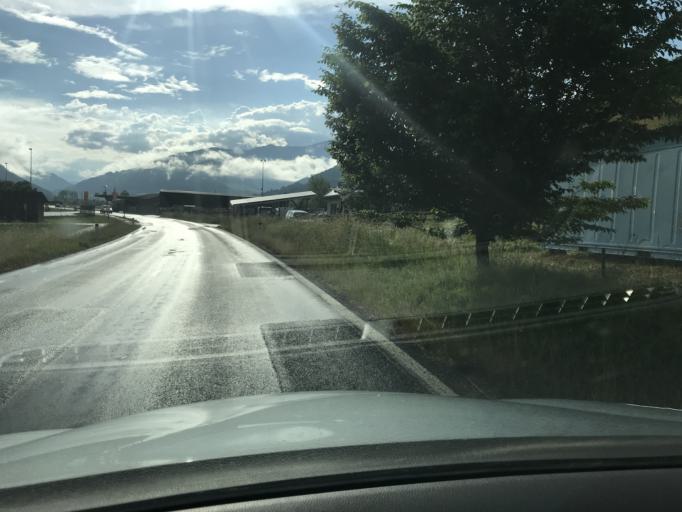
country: AT
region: Styria
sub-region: Politischer Bezirk Murau
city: Sankt Peter am Kammersberg
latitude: 47.1866
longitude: 14.1845
